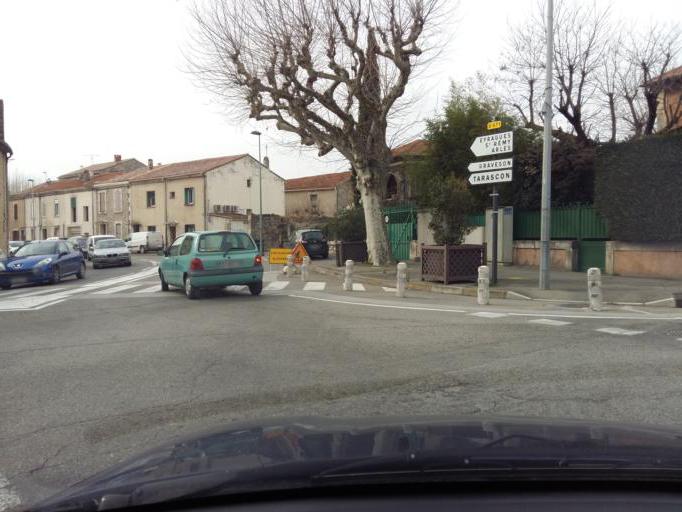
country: FR
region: Provence-Alpes-Cote d'Azur
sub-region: Departement des Bouches-du-Rhone
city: Chateaurenard
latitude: 43.8852
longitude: 4.8496
